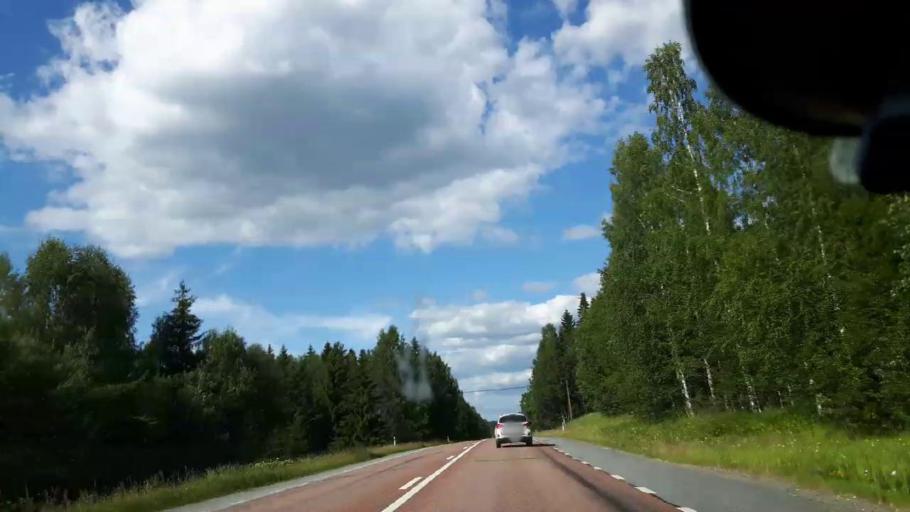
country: SE
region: Jaemtland
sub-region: Braecke Kommun
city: Braecke
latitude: 62.8983
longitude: 15.2644
